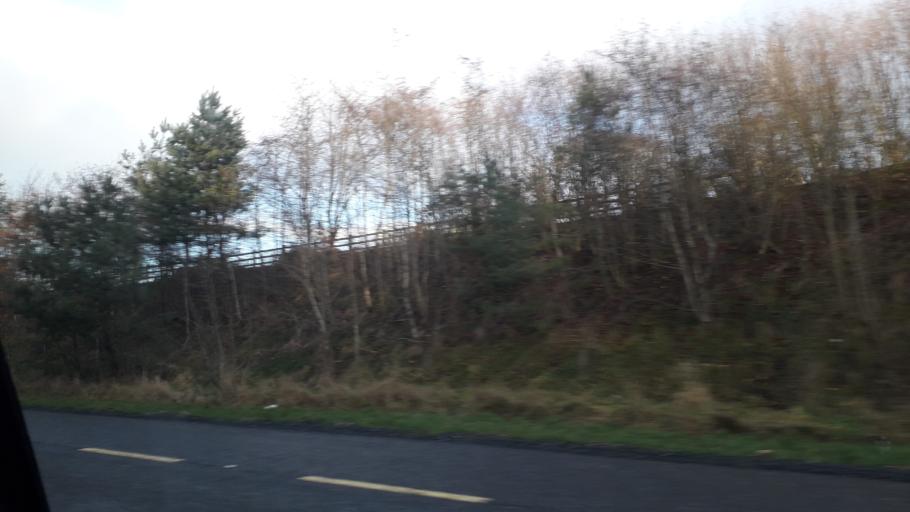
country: IE
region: Ulster
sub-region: County Monaghan
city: Carrickmacross
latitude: 53.9532
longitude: -6.6734
